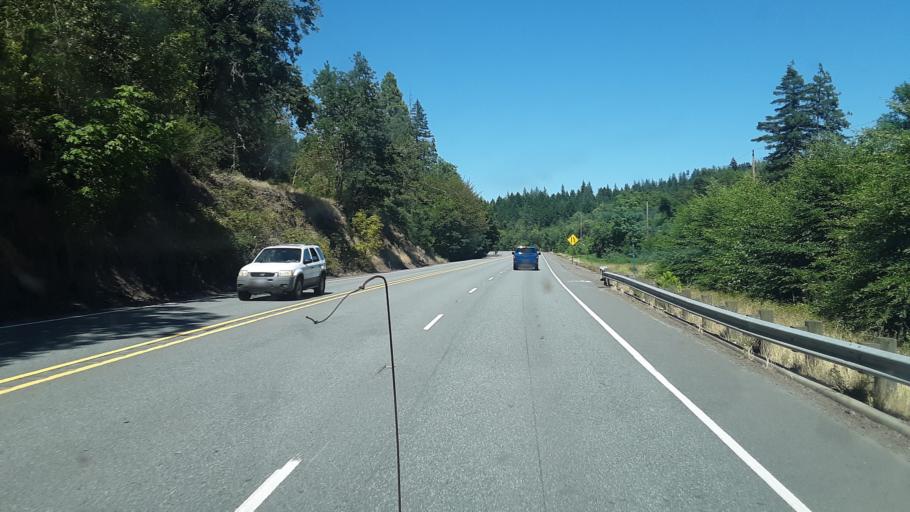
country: US
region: Oregon
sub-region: Josephine County
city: Redwood
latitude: 42.3703
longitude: -123.5048
